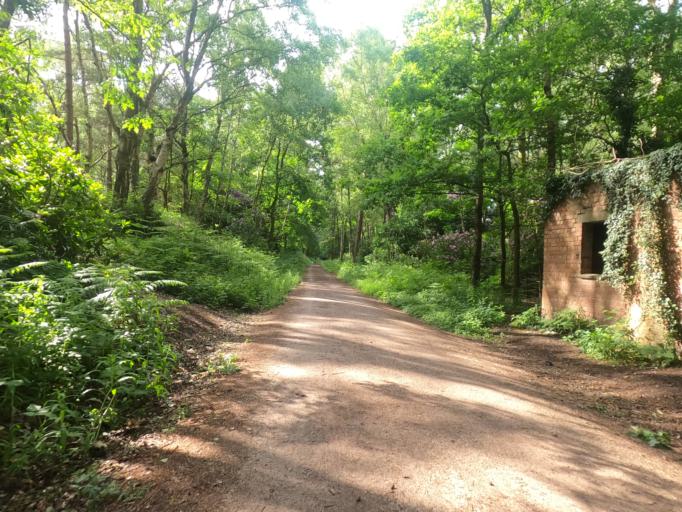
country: GB
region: England
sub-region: Cheshire West and Chester
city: Cuddington
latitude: 53.2190
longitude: -2.6110
